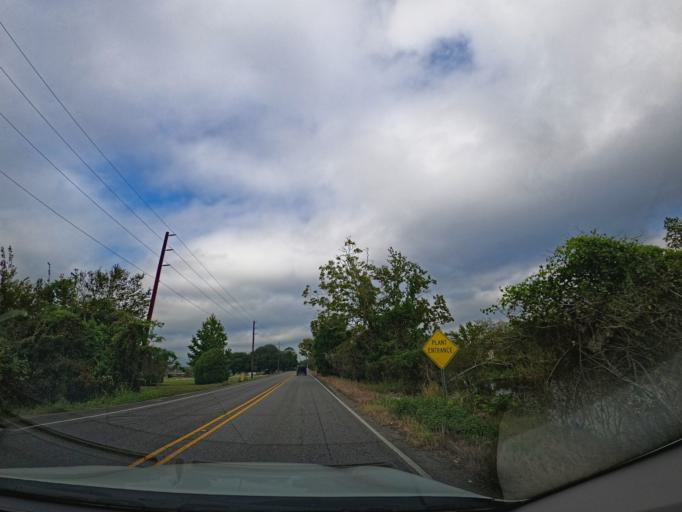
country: US
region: Louisiana
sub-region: Terrebonne Parish
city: Bayou Cane
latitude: 29.6062
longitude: -90.8724
